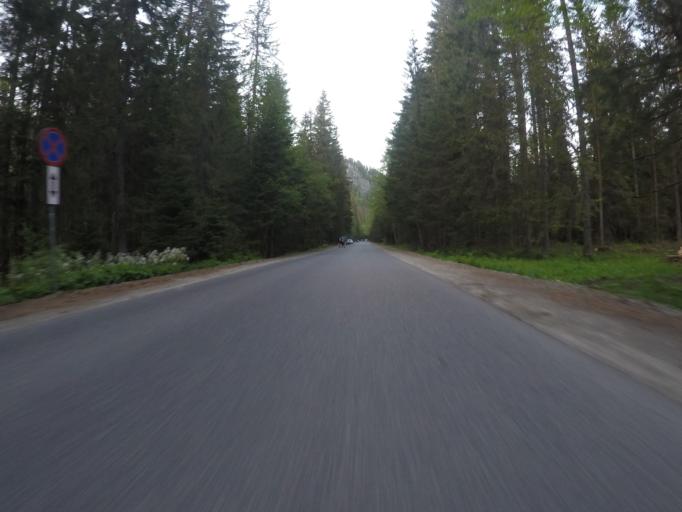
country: PL
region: Lesser Poland Voivodeship
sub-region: Powiat tatrzanski
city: Bukowina Tatrzanska
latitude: 49.2596
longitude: 20.1076
